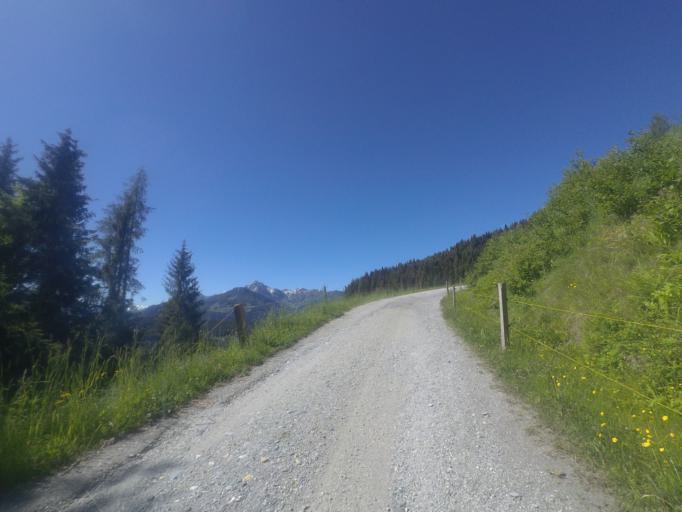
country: AT
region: Salzburg
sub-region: Politischer Bezirk Zell am See
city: Lend
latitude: 47.3274
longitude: 13.0548
